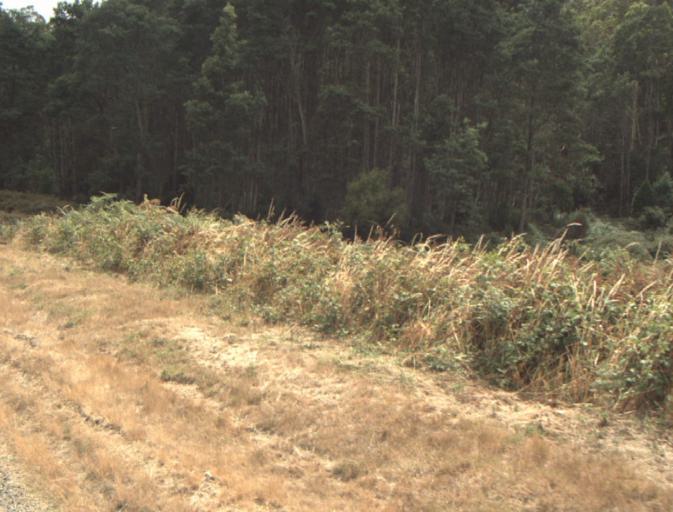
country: AU
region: Tasmania
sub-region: Dorset
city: Bridport
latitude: -41.1821
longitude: 147.2615
